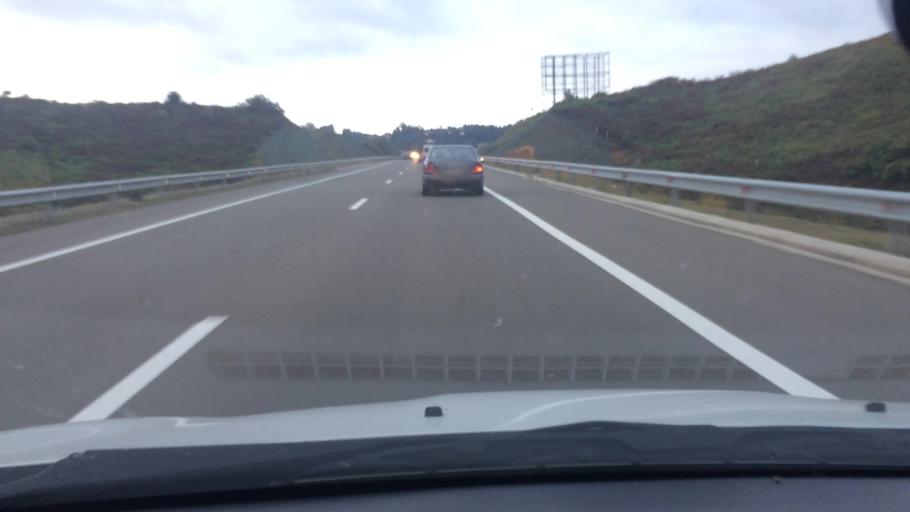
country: GE
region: Ajaria
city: Makhinjauri
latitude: 41.7278
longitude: 41.7509
